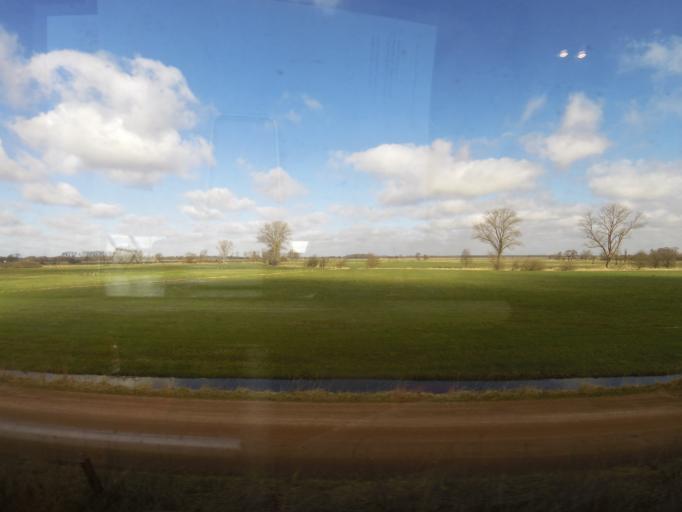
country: DE
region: Lower Saxony
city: Oyten
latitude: 53.0844
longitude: 8.9656
